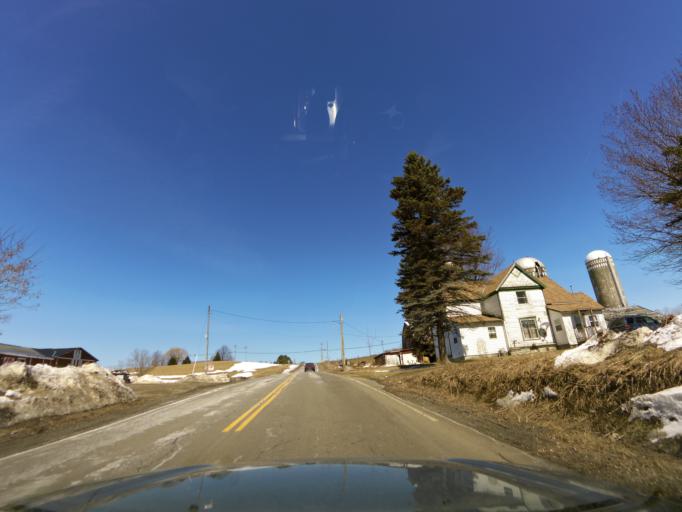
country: US
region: New York
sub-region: Cattaraugus County
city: Yorkshire
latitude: 42.5379
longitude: -78.4565
